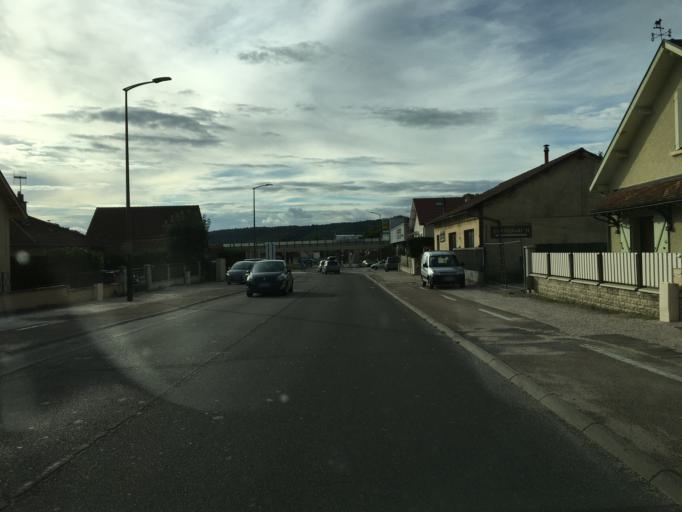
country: FR
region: Bourgogne
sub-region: Departement de la Cote-d'Or
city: Plombieres-les-Dijon
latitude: 47.3349
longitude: 4.9860
